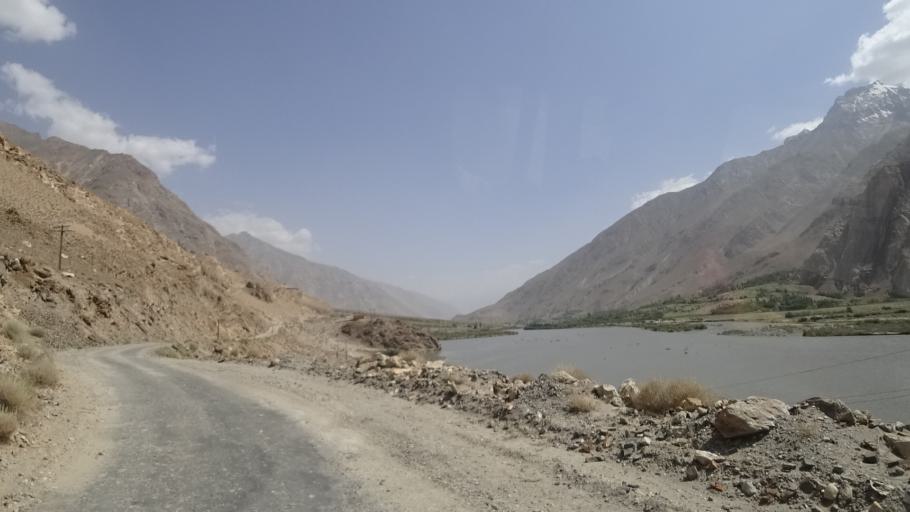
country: TJ
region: Gorno-Badakhshan
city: Ishqoshim
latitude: 36.9345
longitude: 71.4858
